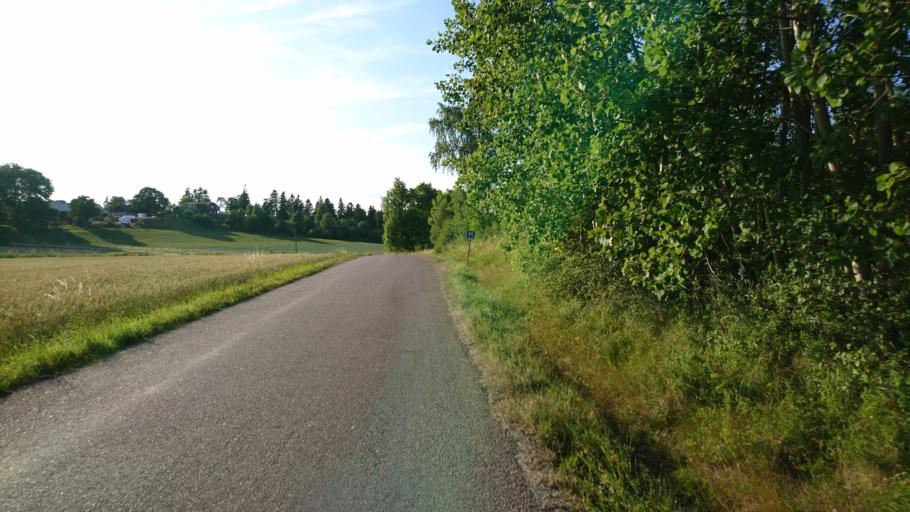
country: SE
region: Soedermanland
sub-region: Strangnas Kommun
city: Stallarholmen
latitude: 59.4015
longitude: 17.2989
